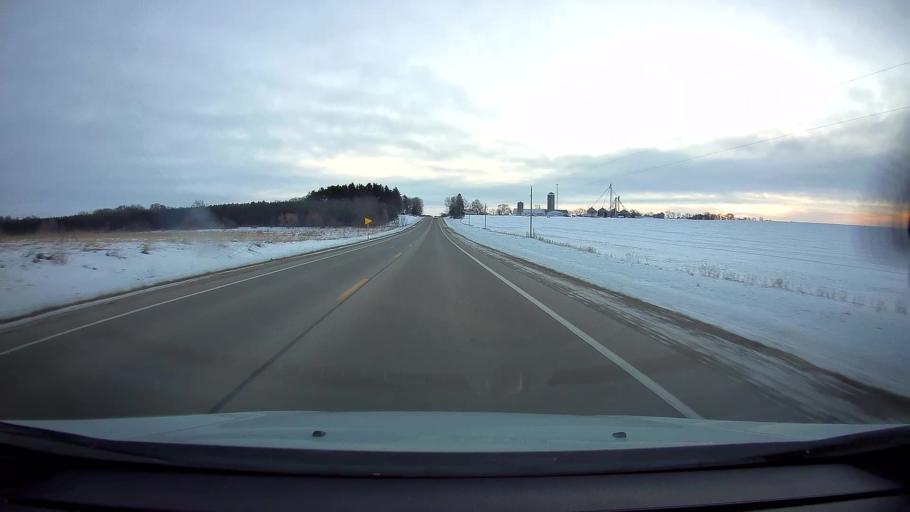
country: US
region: Wisconsin
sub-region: Saint Croix County
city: New Richmond
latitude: 45.1371
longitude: -92.4857
